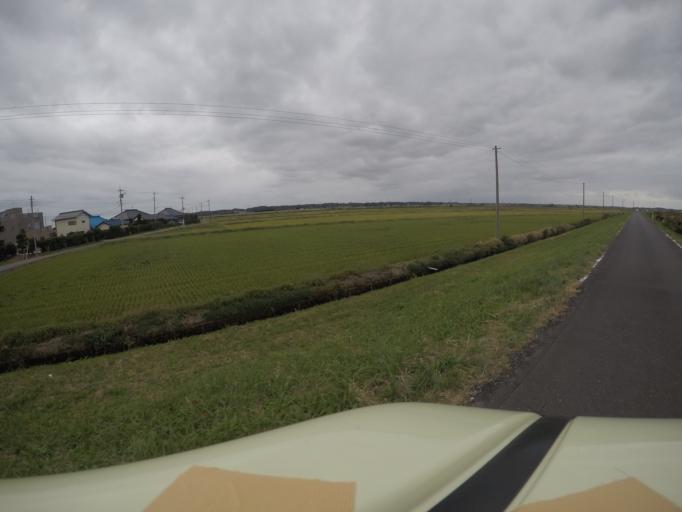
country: JP
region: Ibaraki
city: Inashiki
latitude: 35.9853
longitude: 140.4191
